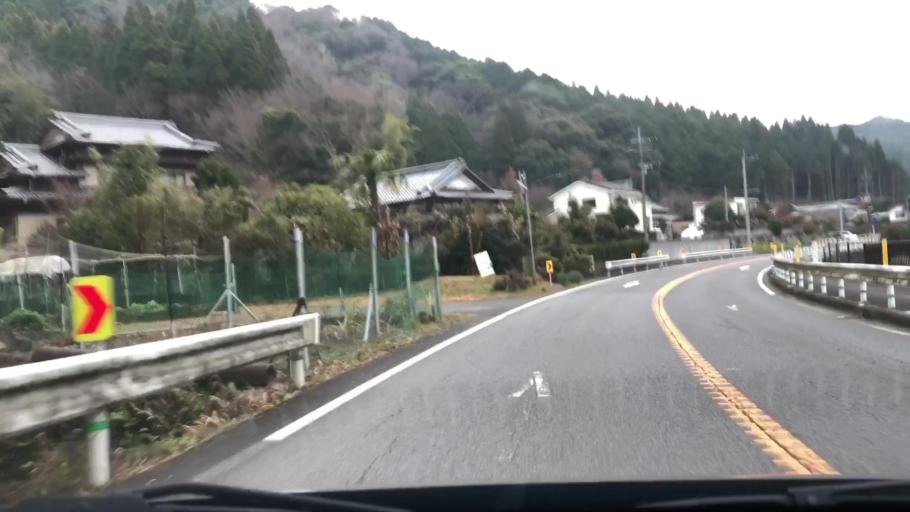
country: JP
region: Oita
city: Usuki
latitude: 33.0098
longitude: 131.7072
